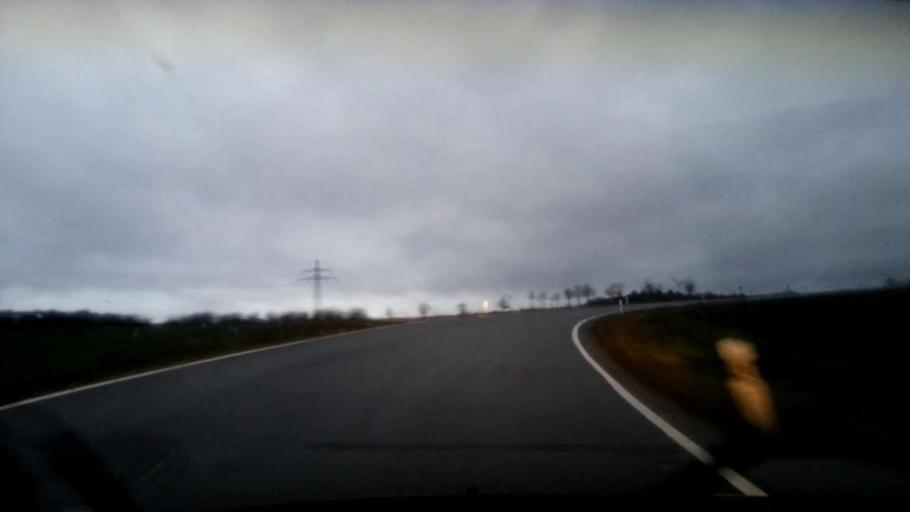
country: DE
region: Bavaria
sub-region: Upper Franconia
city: Poxdorf
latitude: 49.9677
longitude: 11.1297
